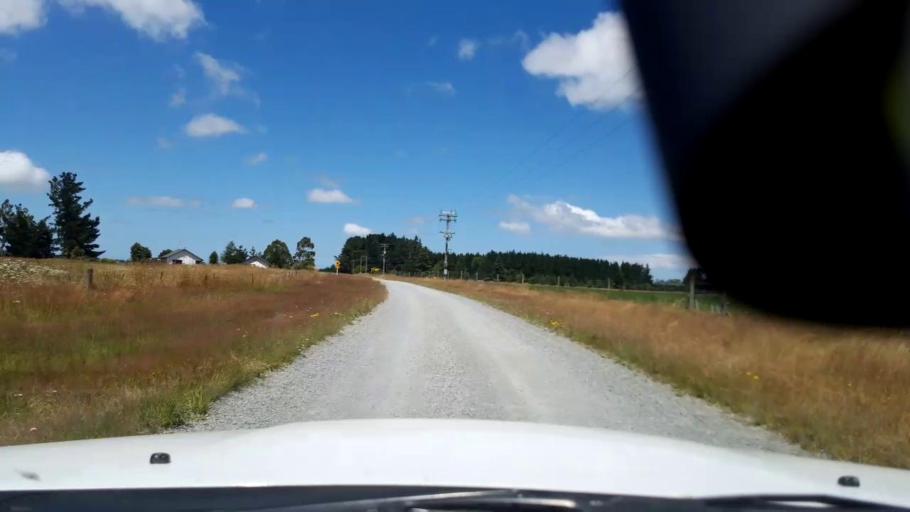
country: NZ
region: Canterbury
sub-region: Timaru District
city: Pleasant Point
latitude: -43.9927
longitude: 171.2930
